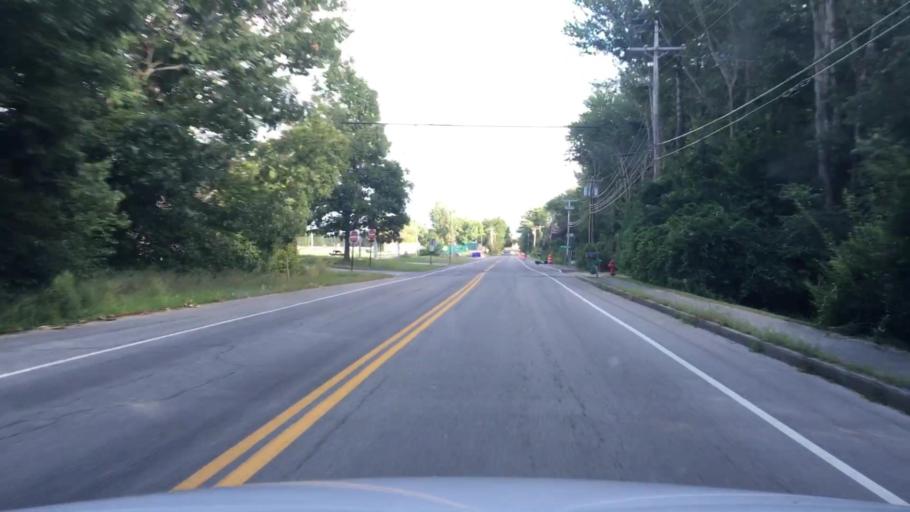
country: US
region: Maine
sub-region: York County
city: Eliot
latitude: 43.1260
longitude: -70.8382
